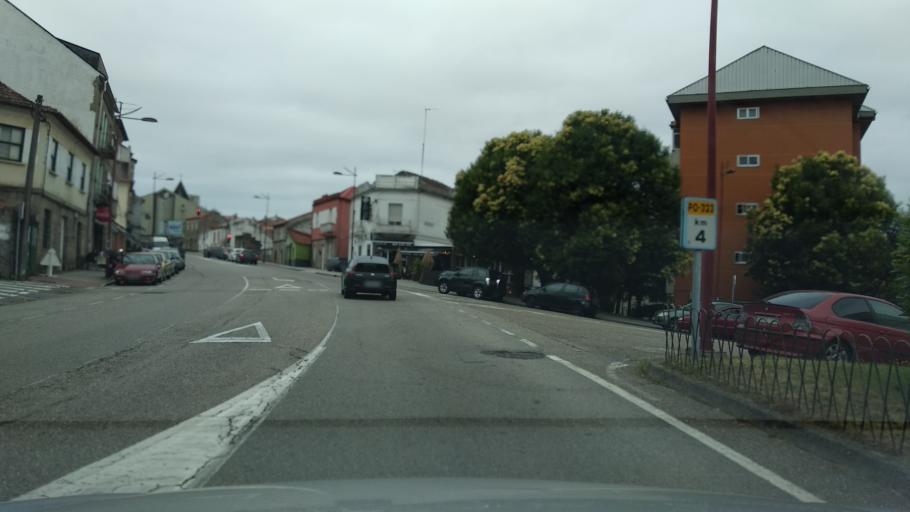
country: ES
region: Galicia
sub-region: Provincia de Pontevedra
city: Vigo
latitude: 42.2514
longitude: -8.6925
